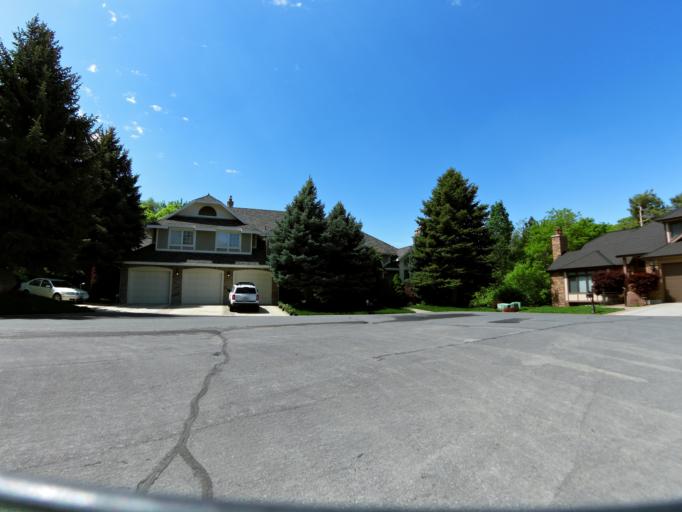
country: US
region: Utah
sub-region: Weber County
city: Uintah
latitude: 41.1773
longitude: -111.9365
